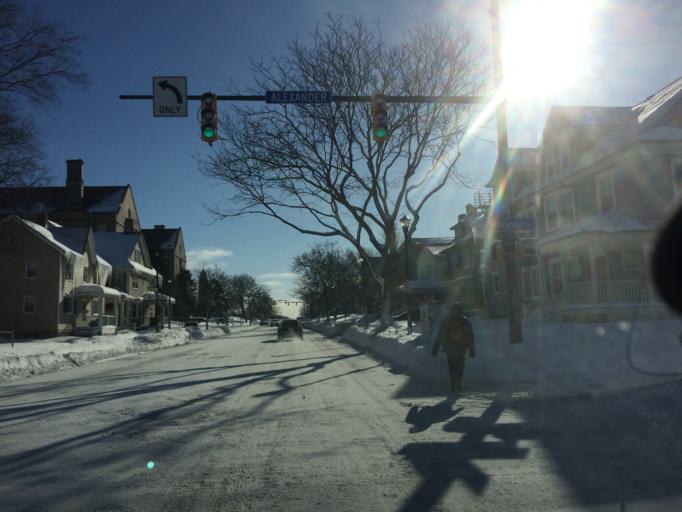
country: US
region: New York
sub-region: Monroe County
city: Rochester
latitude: 43.1583
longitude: -77.5930
